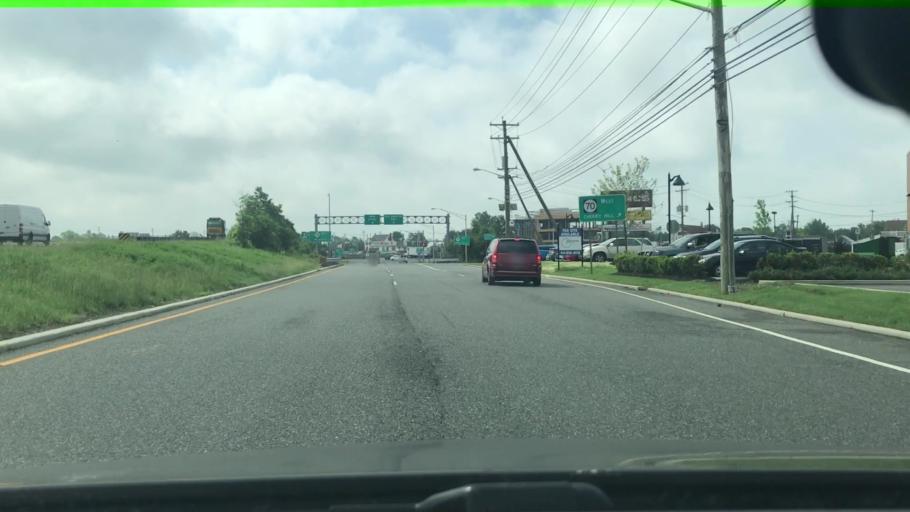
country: US
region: New Jersey
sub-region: Burlington County
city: Marlton
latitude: 39.8960
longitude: -74.9298
